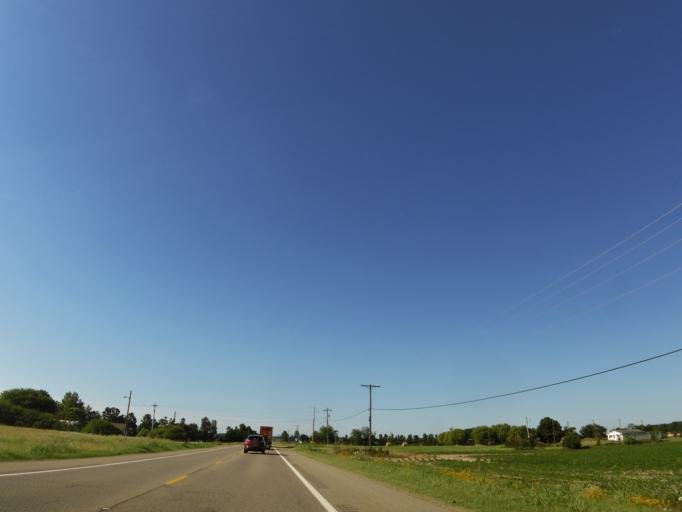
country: US
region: Arkansas
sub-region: Clay County
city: Corning
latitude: 36.4414
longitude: -90.5857
